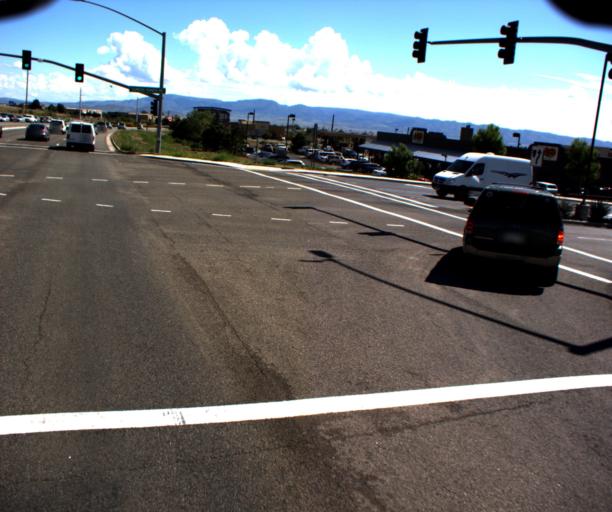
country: US
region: Arizona
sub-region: Yavapai County
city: Prescott Valley
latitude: 34.5761
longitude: -112.3654
